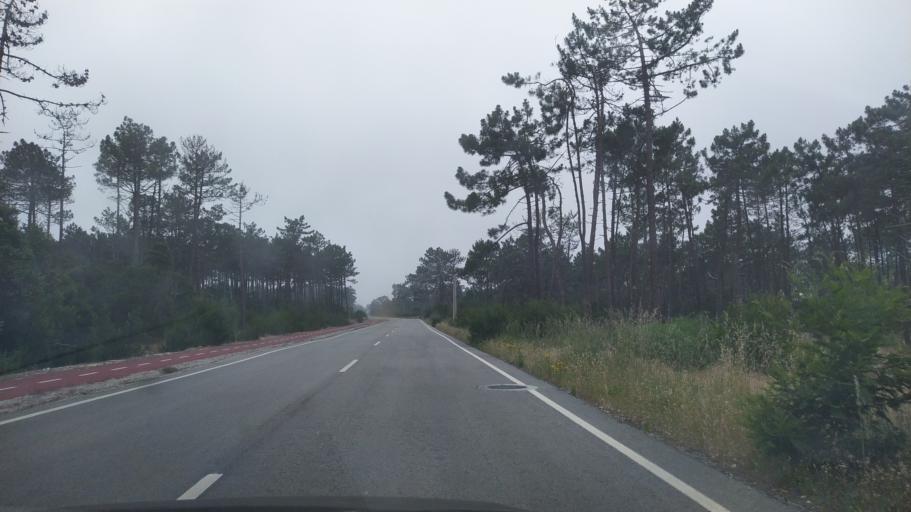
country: PT
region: Aveiro
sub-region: Ilhavo
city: Gafanha da Encarnacao
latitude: 40.5702
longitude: -8.7375
